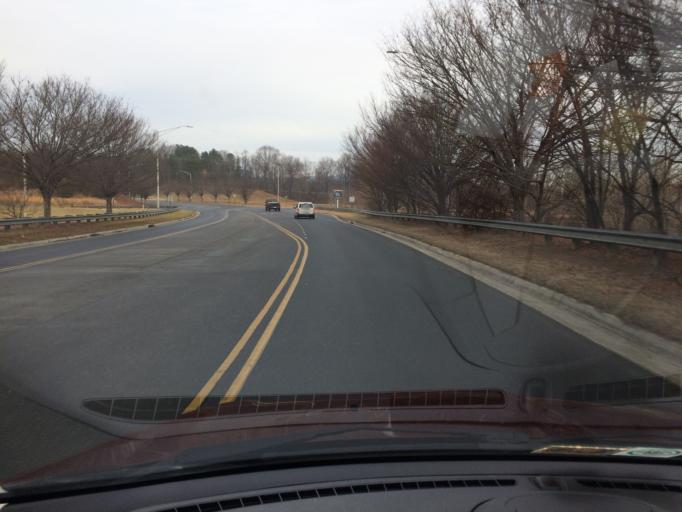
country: US
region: Virginia
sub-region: City of Bedford
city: Bedford
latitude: 37.3368
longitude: -79.4964
